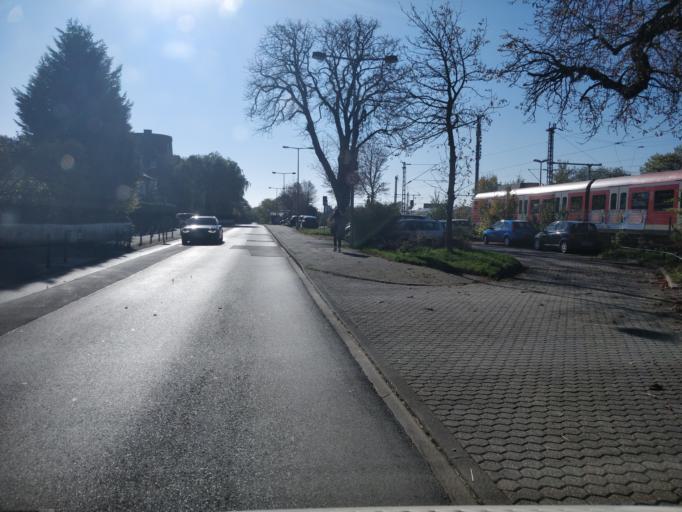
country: DE
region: North Rhine-Westphalia
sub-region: Regierungsbezirk Koln
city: Sinnersdorf
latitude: 51.0521
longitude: 6.8525
